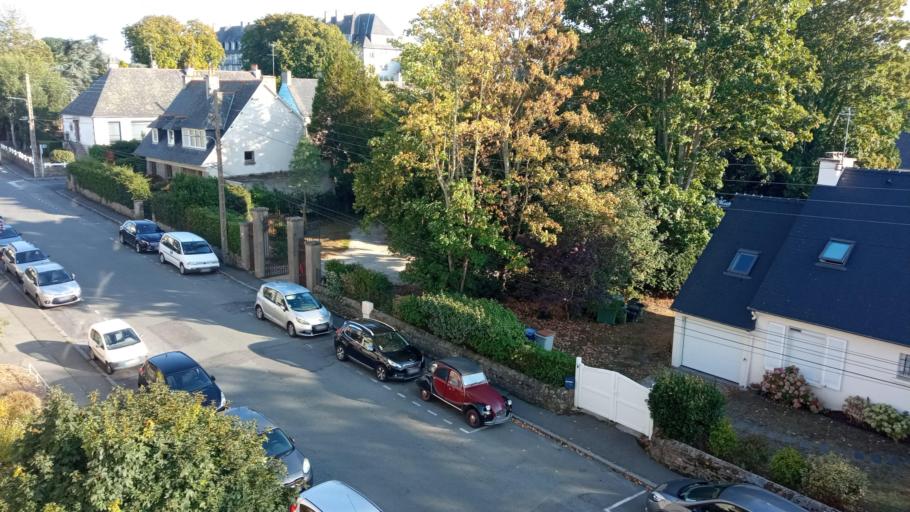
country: FR
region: Brittany
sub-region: Departement d'Ille-et-Vilaine
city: Saint-Malo
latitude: 48.6323
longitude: -2.0156
